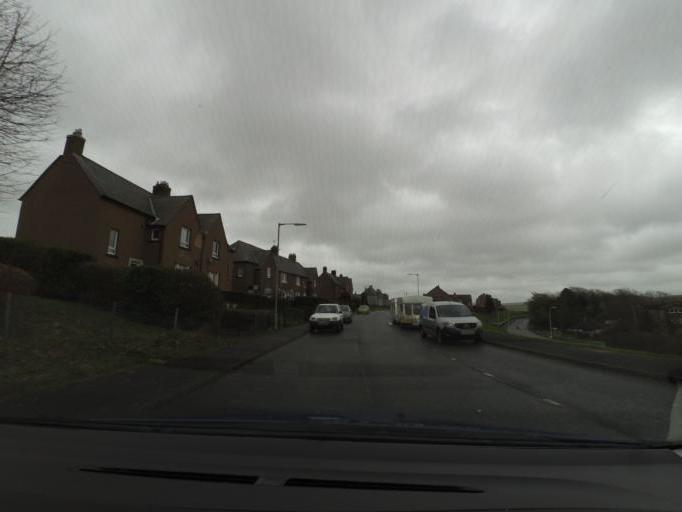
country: GB
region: Scotland
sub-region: The Scottish Borders
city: Hawick
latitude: 55.4345
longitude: -2.7740
